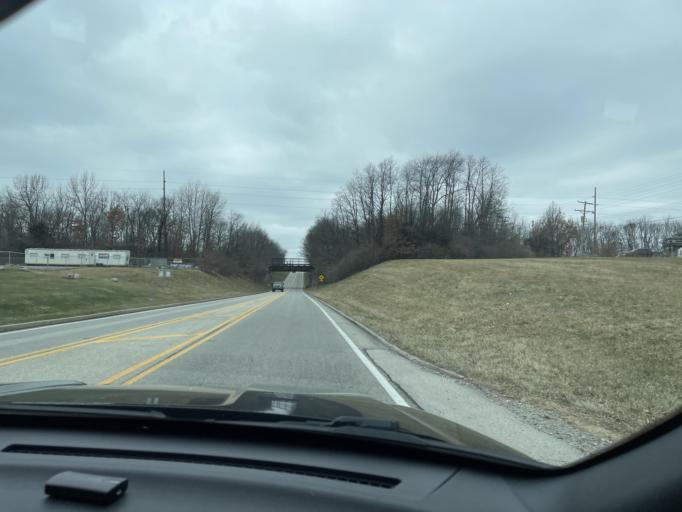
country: US
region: Illinois
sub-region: Sangamon County
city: Leland Grove
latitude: 39.8180
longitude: -89.7087
